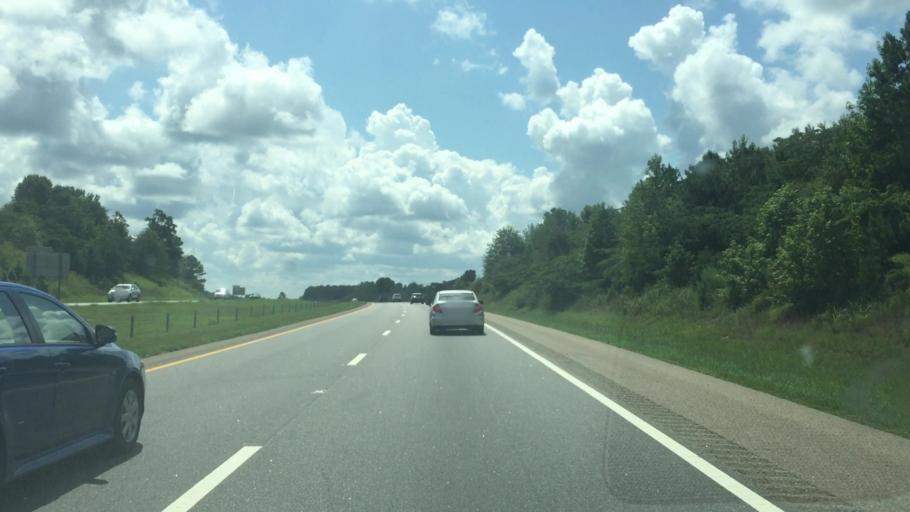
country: US
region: North Carolina
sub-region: Richmond County
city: Cordova
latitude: 34.9377
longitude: -79.8410
